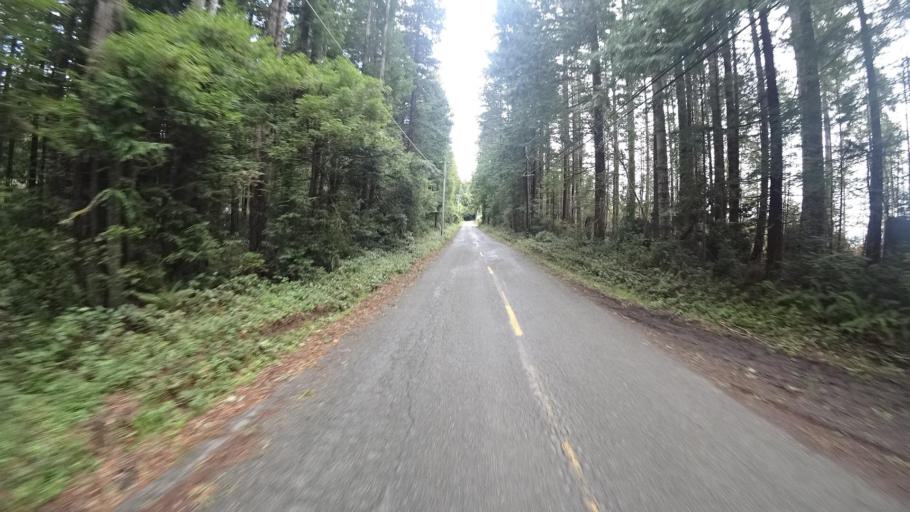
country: US
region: California
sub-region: Humboldt County
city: Bayside
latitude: 40.7832
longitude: -124.0105
